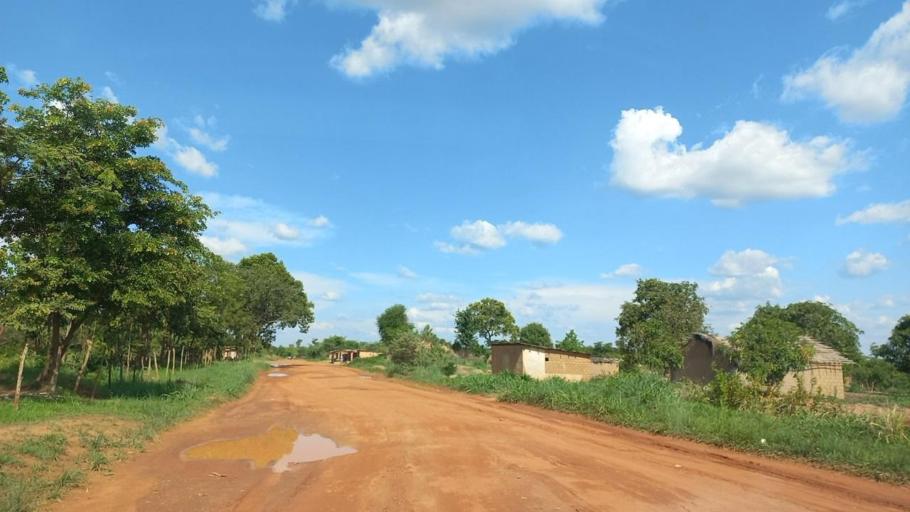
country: ZM
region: Copperbelt
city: Kitwe
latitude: -12.8659
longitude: 28.3708
